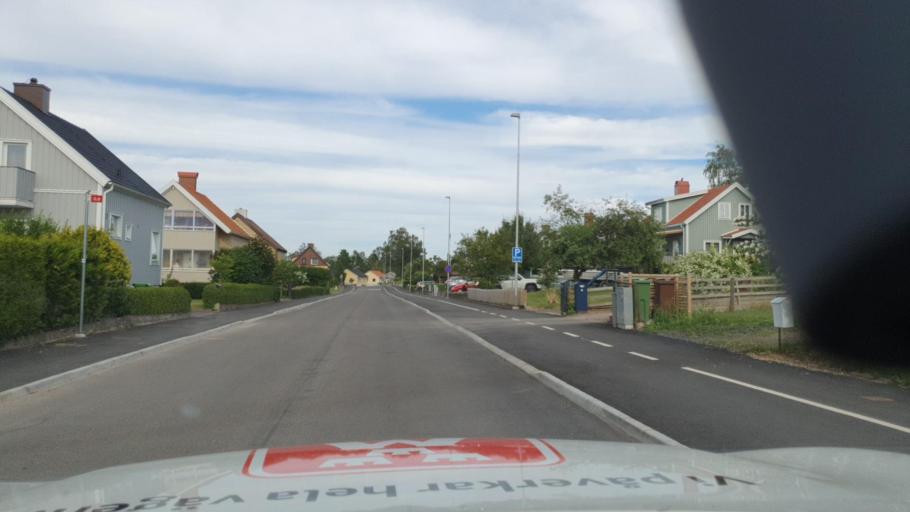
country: SE
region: Vaestra Goetaland
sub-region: Skovde Kommun
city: Skoevde
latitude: 58.3916
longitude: 13.8678
